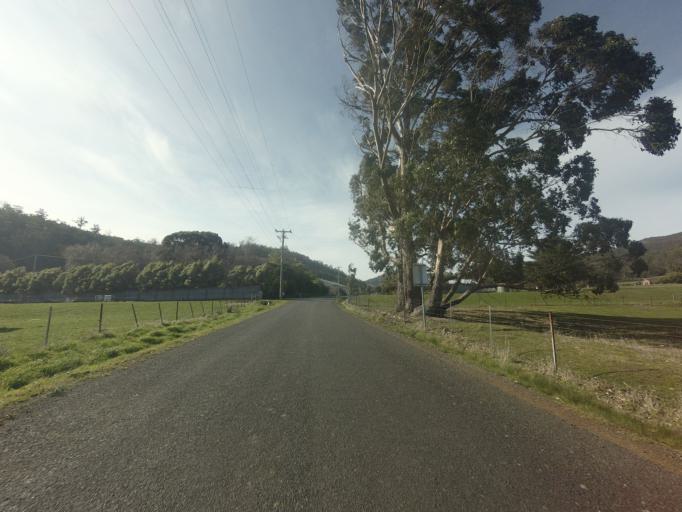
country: AU
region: Tasmania
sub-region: Huon Valley
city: Cygnet
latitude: -43.1796
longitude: 147.1323
